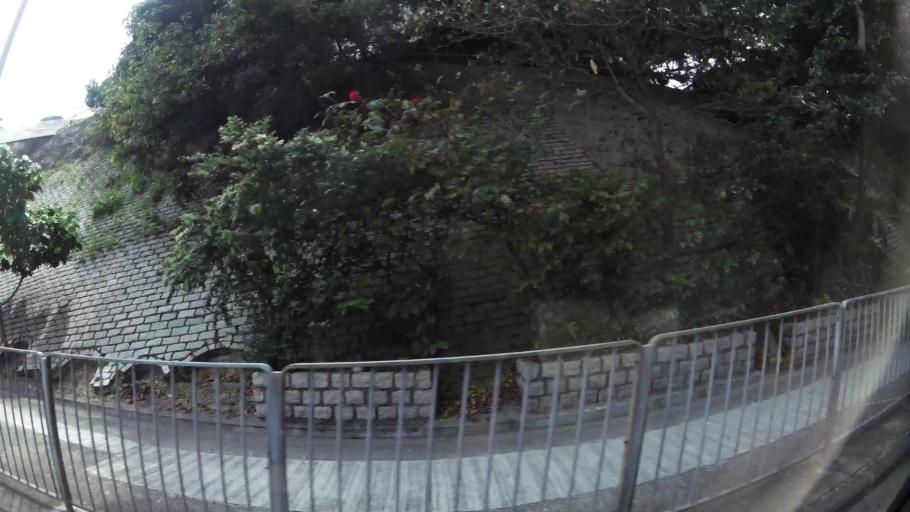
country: HK
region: Kowloon City
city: Kowloon
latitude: 22.2902
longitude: 114.2080
